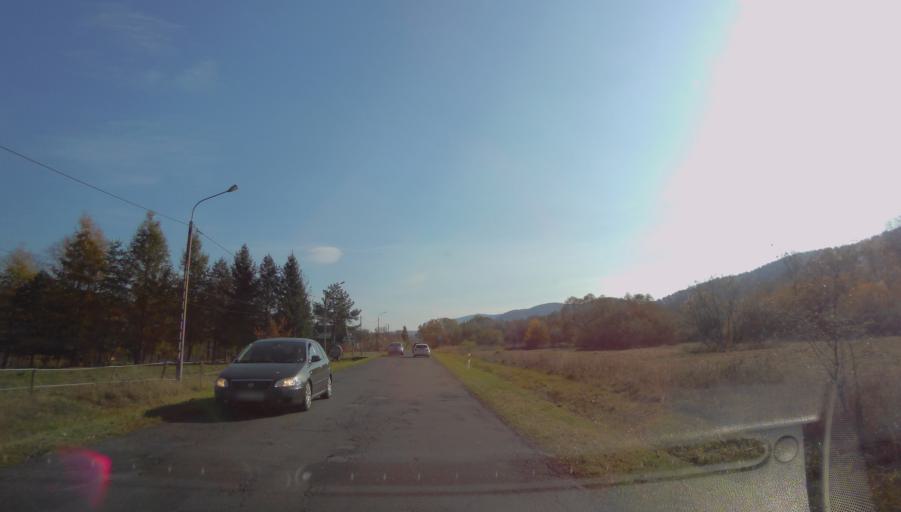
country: PL
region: Subcarpathian Voivodeship
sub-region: Powiat sanocki
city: Rzepedz
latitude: 49.2291
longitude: 22.1656
